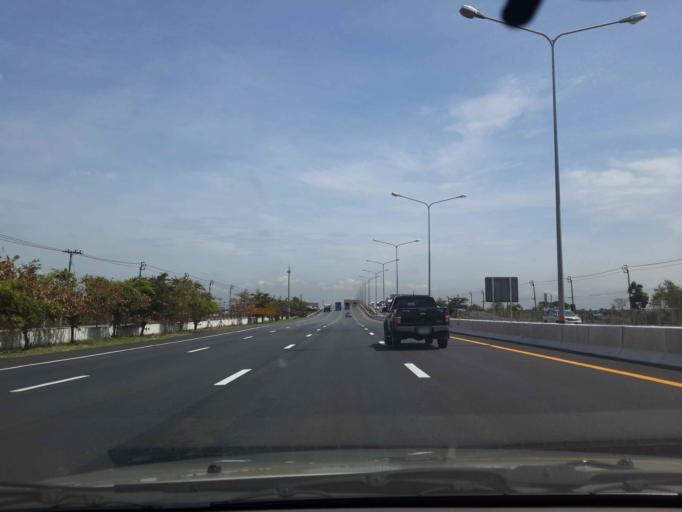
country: TH
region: Bangkok
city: Lat Krabang
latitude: 13.7227
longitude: 100.8139
